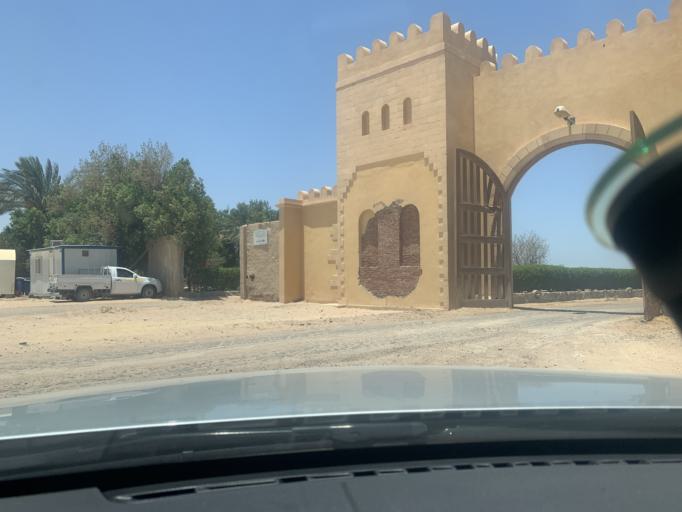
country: EG
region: Red Sea
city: El Gouna
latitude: 27.3959
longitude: 33.6488
